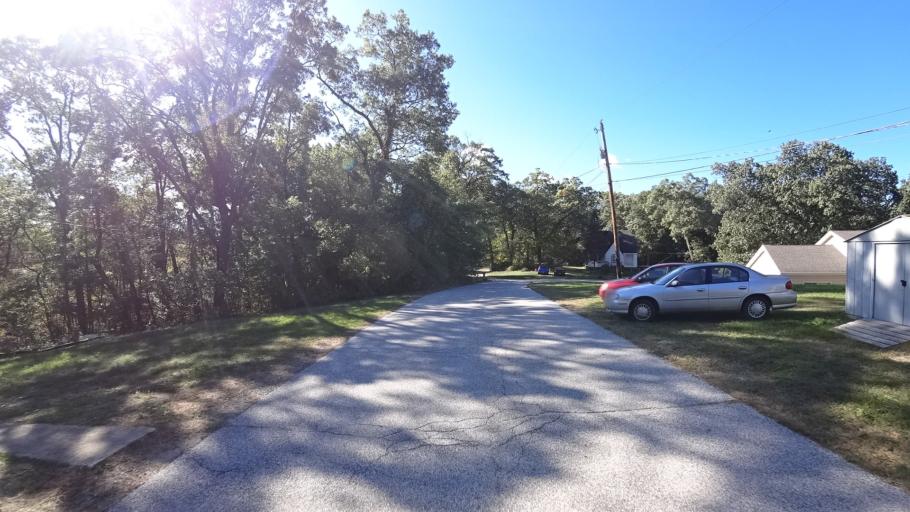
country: US
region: Indiana
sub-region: LaPorte County
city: Michigan City
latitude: 41.6931
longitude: -86.9287
